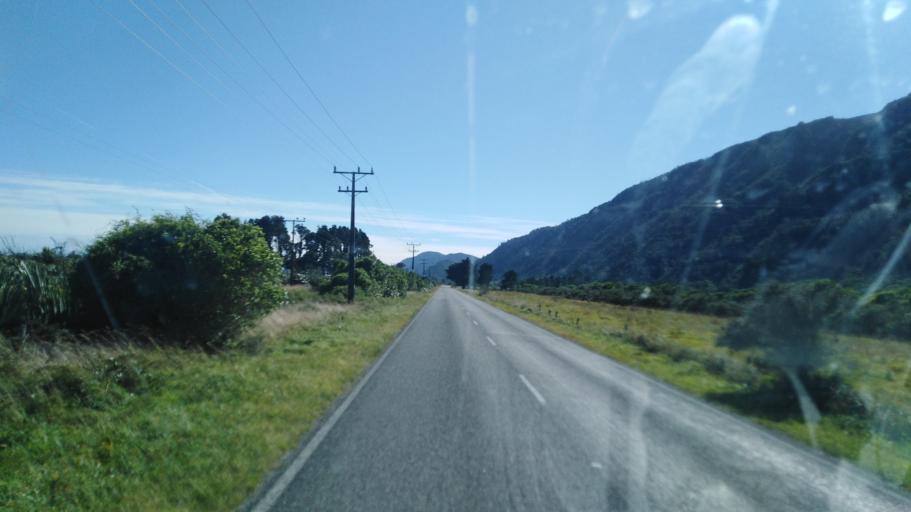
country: NZ
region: West Coast
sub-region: Buller District
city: Westport
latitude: -41.6547
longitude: 171.8253
